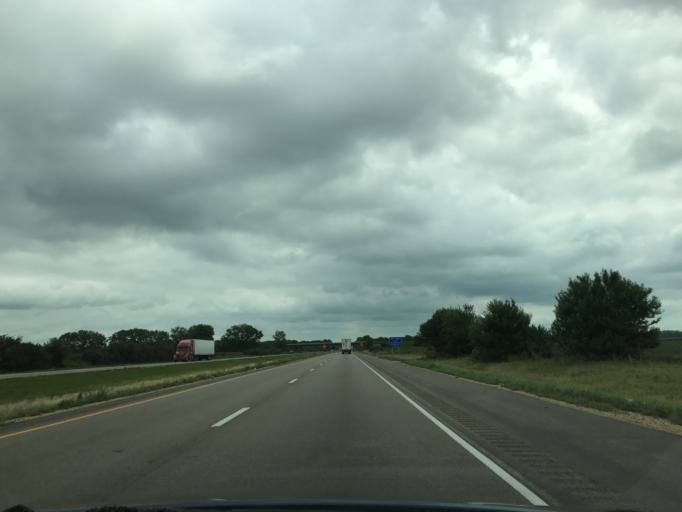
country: US
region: Illinois
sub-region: Bureau County
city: Princeton
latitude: 41.3945
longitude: -89.5937
